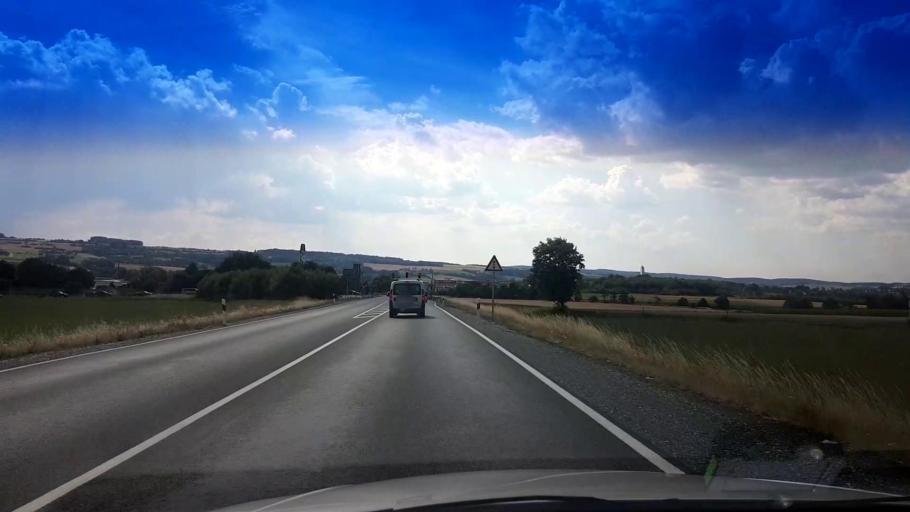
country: DE
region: Bavaria
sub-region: Upper Franconia
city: Himmelkron
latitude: 50.0553
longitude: 11.6230
